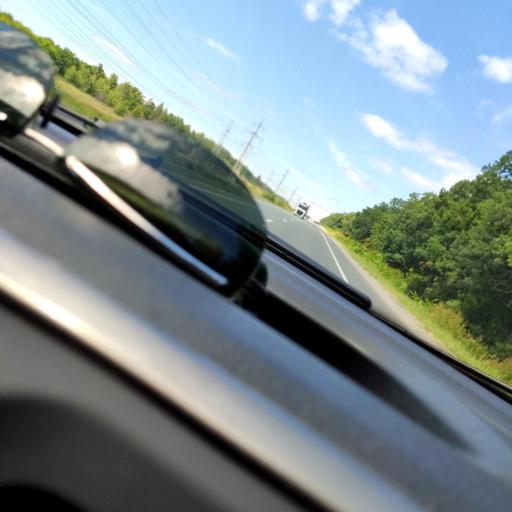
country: RU
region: Samara
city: Bogatyr'
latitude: 53.4969
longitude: 49.9604
